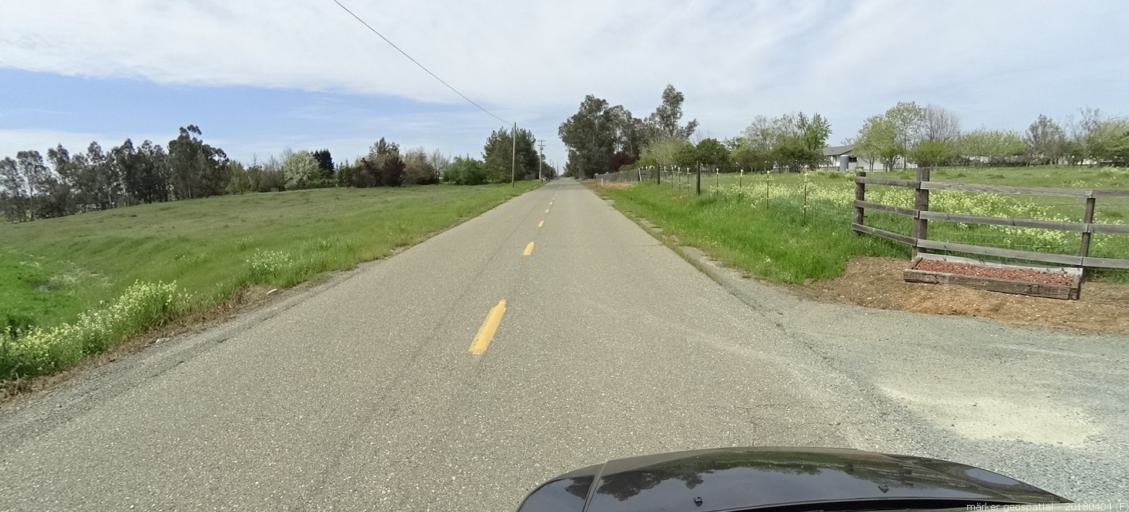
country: US
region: California
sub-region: Sacramento County
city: Clay
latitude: 38.3142
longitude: -121.1470
